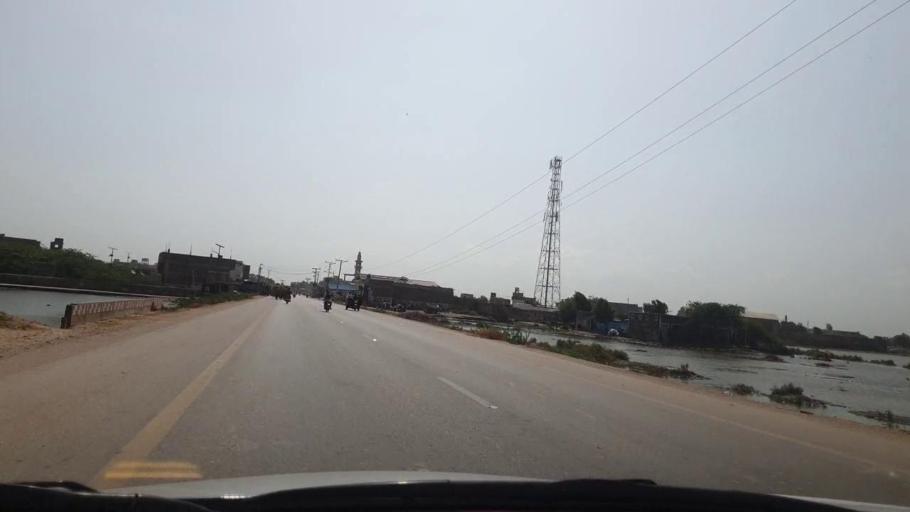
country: PK
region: Sindh
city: Matli
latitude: 25.0361
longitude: 68.6529
